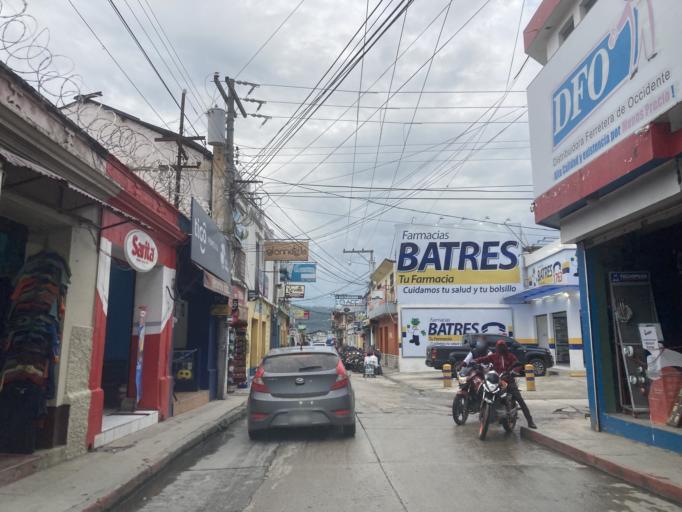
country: GT
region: Huehuetenango
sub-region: Municipio de Huehuetenango
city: Huehuetenango
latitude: 15.3223
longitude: -91.4686
